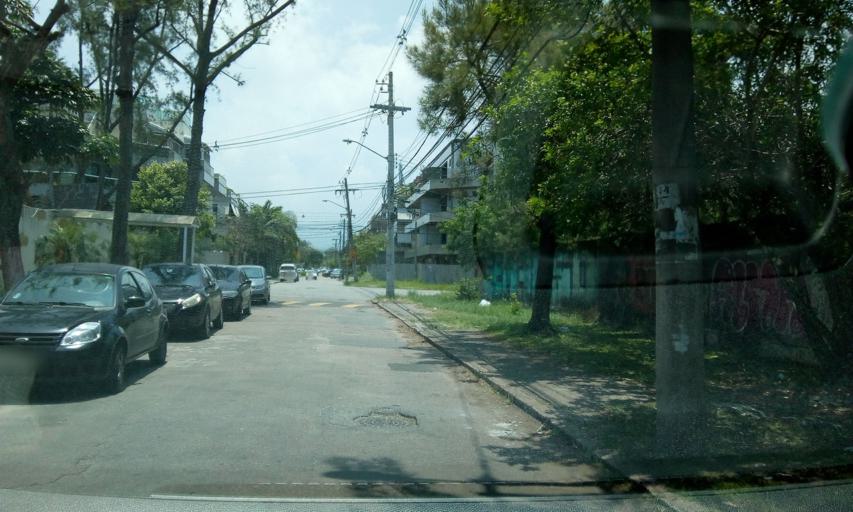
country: BR
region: Rio de Janeiro
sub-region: Nilopolis
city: Nilopolis
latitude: -23.0215
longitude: -43.4732
